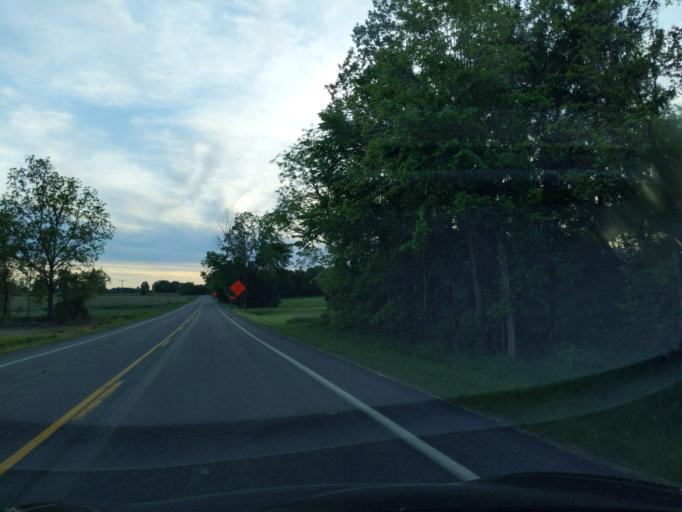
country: US
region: Michigan
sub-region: Ingham County
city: Mason
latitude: 42.6007
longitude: -84.3506
